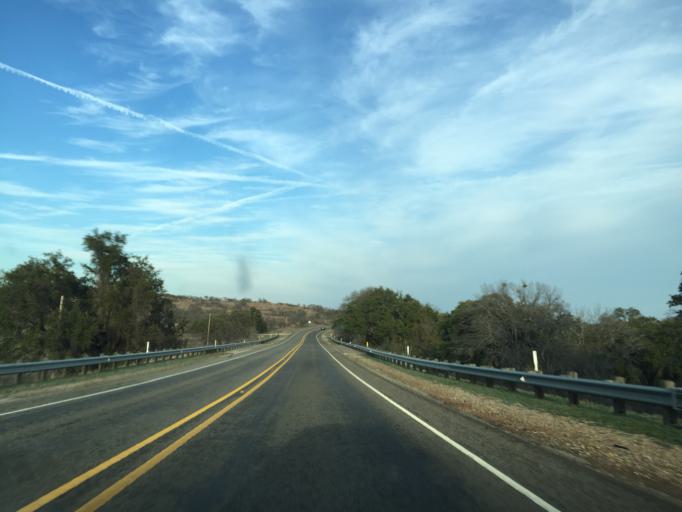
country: US
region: Texas
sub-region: Llano County
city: Llano
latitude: 30.7619
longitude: -98.6158
